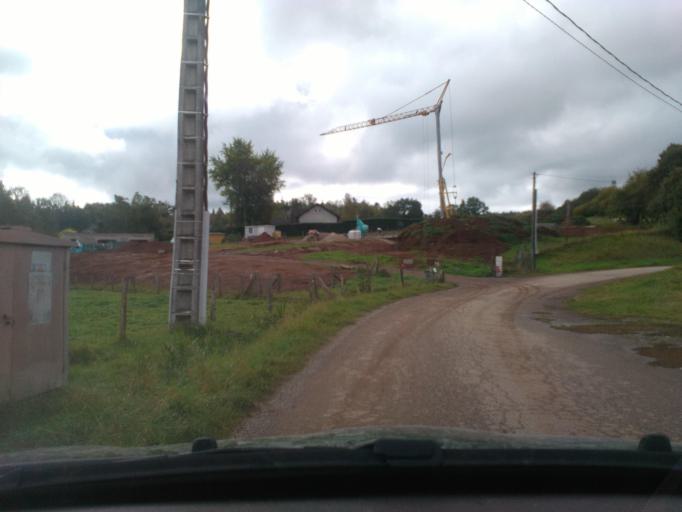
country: FR
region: Lorraine
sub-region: Departement des Vosges
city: Etival-Clairefontaine
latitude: 48.3554
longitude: 6.8537
